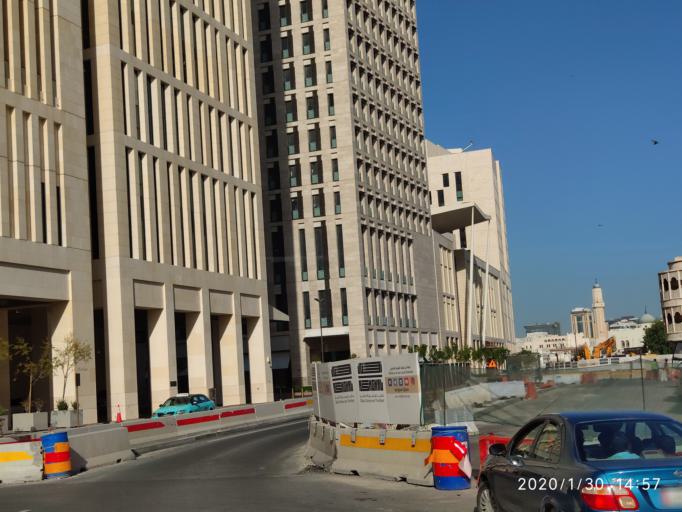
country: QA
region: Baladiyat ad Dawhah
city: Doha
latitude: 25.2835
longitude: 51.5273
